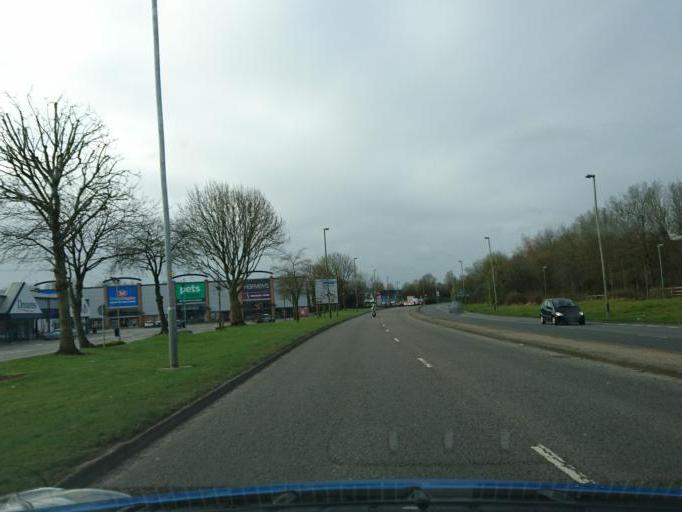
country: GB
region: England
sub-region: Borough of Swindon
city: Swindon
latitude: 51.5579
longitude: -1.8137
